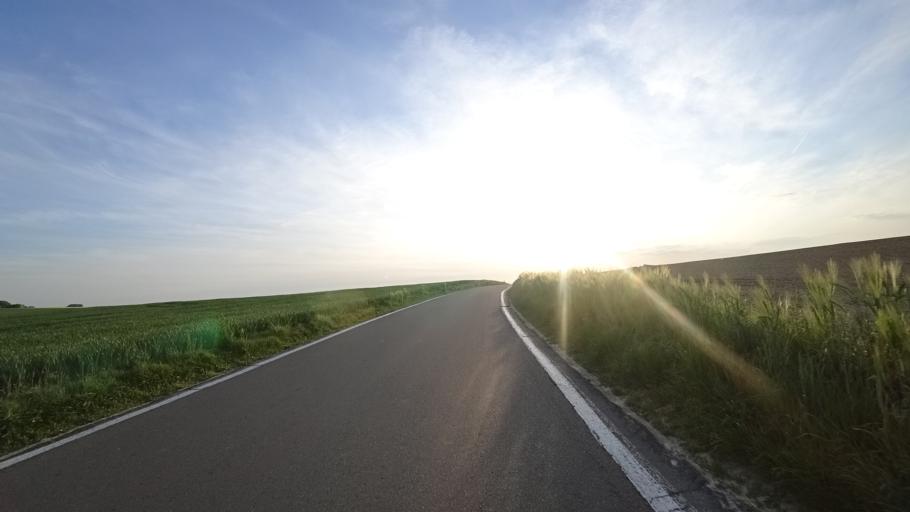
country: BE
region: Wallonia
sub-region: Province du Brabant Wallon
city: Walhain-Saint-Paul
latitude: 50.6407
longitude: 4.7023
